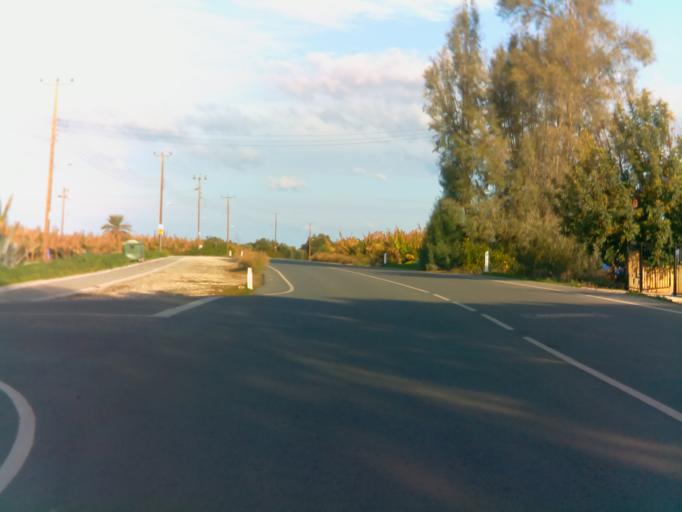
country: CY
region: Pafos
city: Pegeia
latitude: 34.8929
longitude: 32.3353
